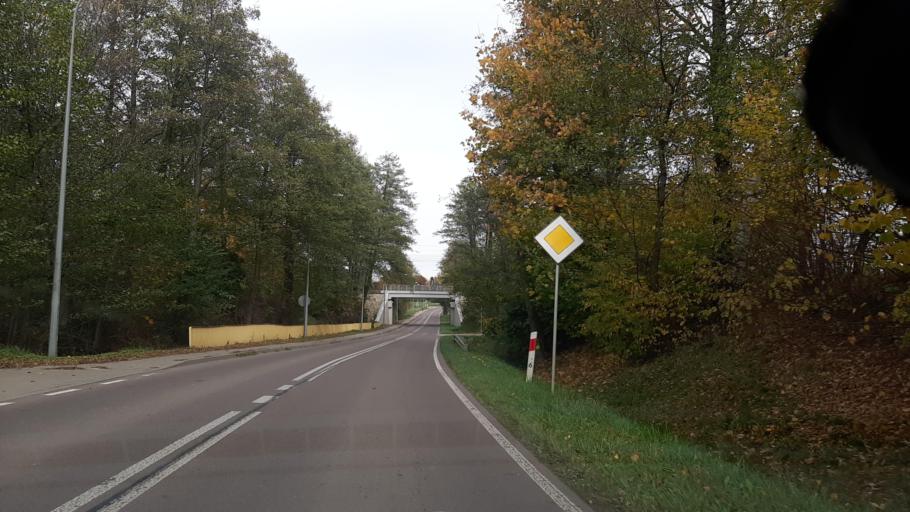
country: PL
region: Lublin Voivodeship
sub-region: Powiat pulawski
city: Naleczow
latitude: 51.3161
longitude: 22.2214
